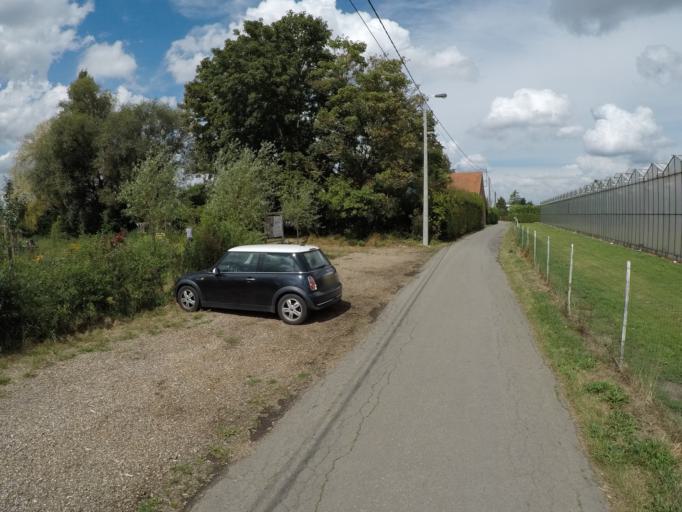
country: BE
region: Flanders
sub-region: Provincie Antwerpen
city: Wommelgem
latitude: 51.1869
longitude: 4.5328
